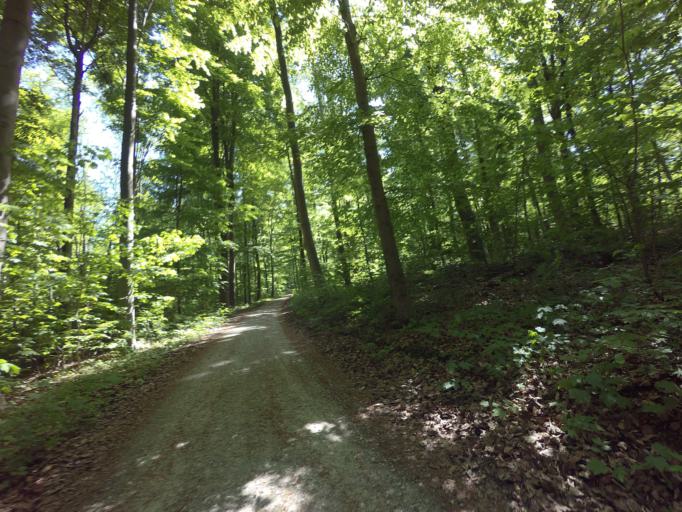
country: DE
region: Lower Saxony
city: Hildesheim
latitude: 52.1386
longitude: 9.9881
